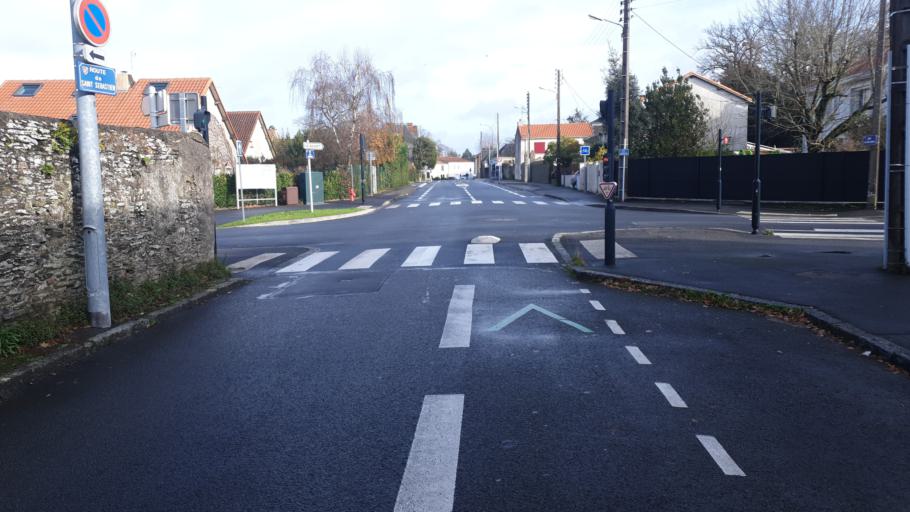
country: FR
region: Pays de la Loire
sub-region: Departement de la Loire-Atlantique
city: Saint-Sebastien-sur-Loire
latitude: 47.2002
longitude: -1.5268
